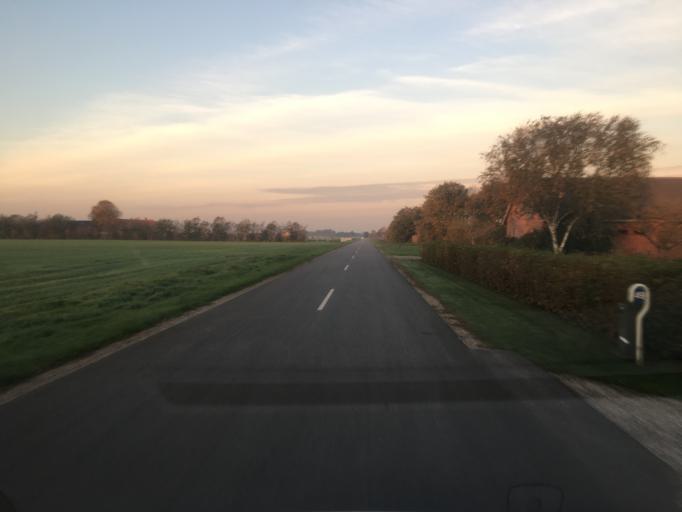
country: DK
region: South Denmark
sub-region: Tonder Kommune
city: Logumkloster
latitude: 55.0620
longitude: 9.0130
